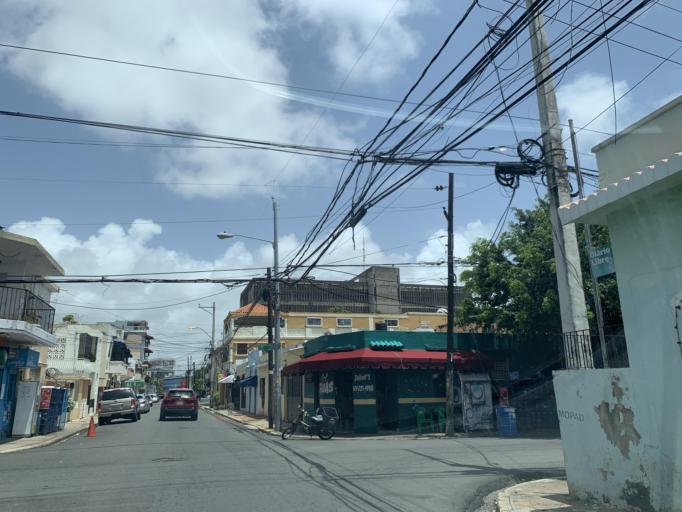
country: DO
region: Nacional
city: San Carlos
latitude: 18.4779
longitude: -69.9045
